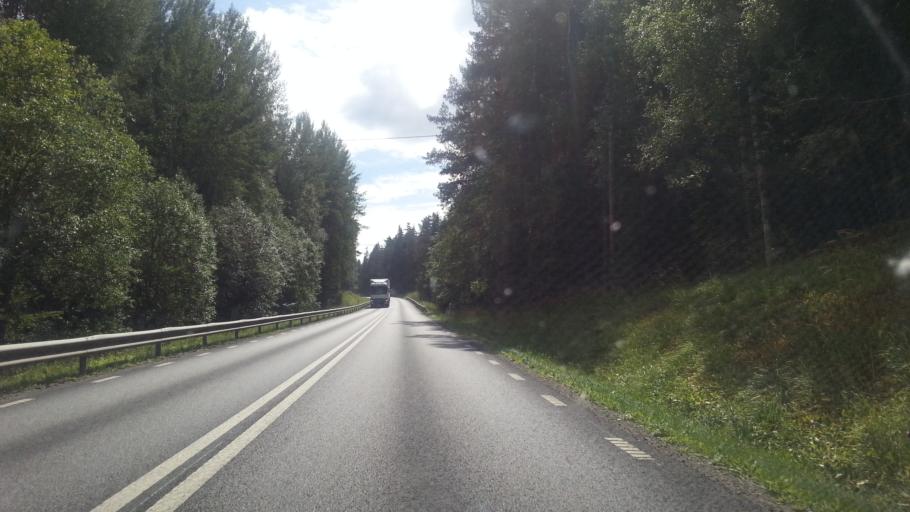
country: SE
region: OErebro
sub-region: Lindesbergs Kommun
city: Stora
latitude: 59.6570
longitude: 15.1060
